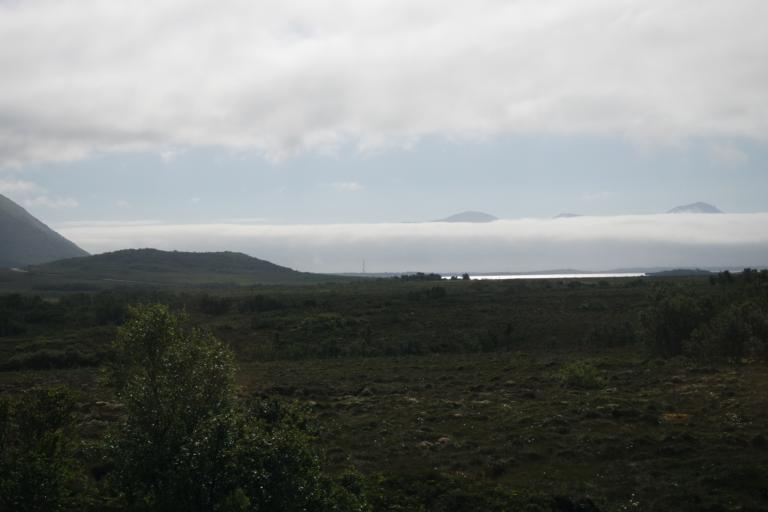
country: NO
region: Nordland
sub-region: Sortland
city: Sortland
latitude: 69.0142
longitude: 15.5145
